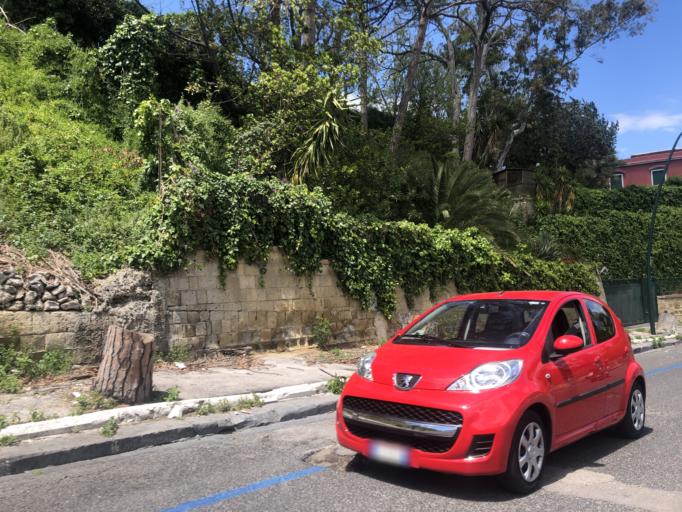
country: IT
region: Campania
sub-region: Provincia di Napoli
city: Bagnoli
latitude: 40.8000
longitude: 14.1839
